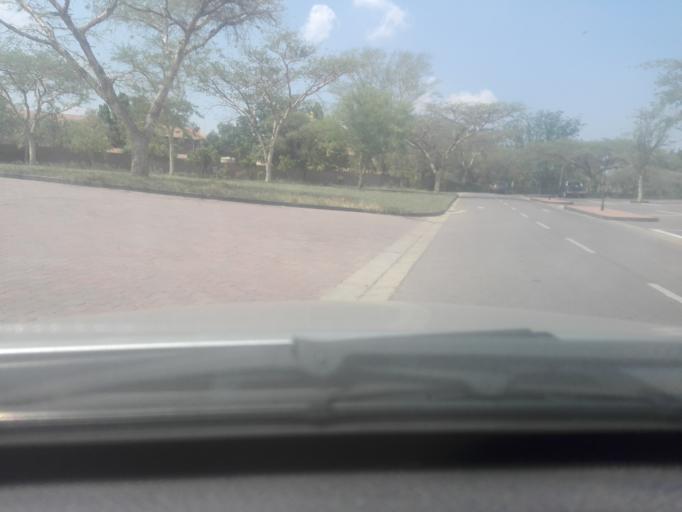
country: BW
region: Kweneng
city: Mogoditshane
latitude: -24.6394
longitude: 25.8762
